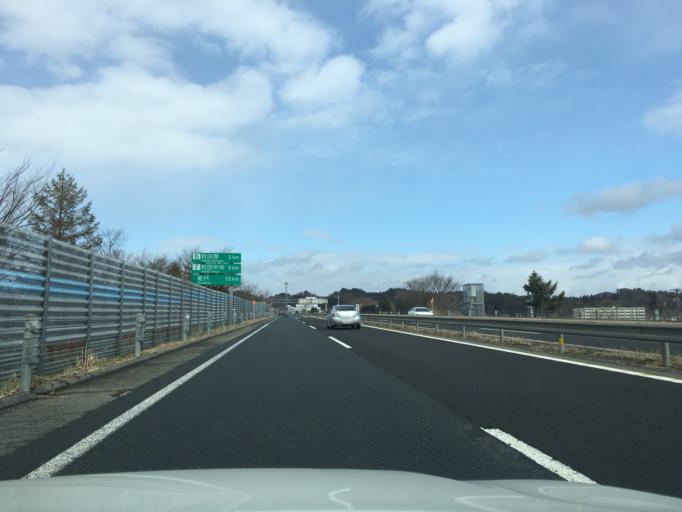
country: JP
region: Akita
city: Akita
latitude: 39.6466
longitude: 140.2080
